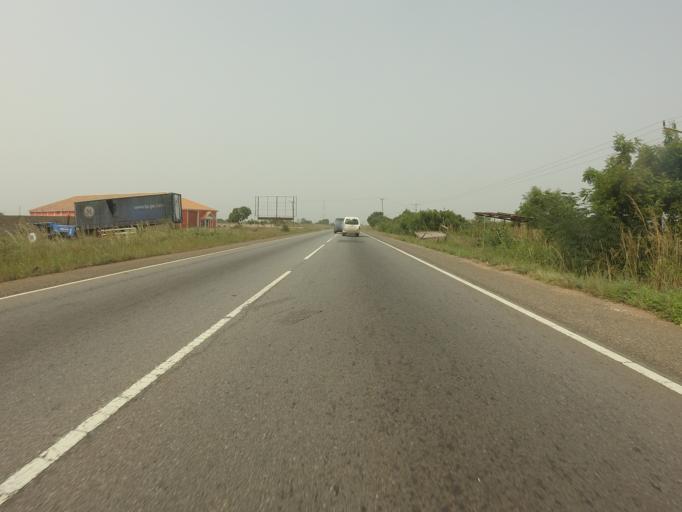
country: GH
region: Volta
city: Anloga
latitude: 5.9285
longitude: 0.5232
